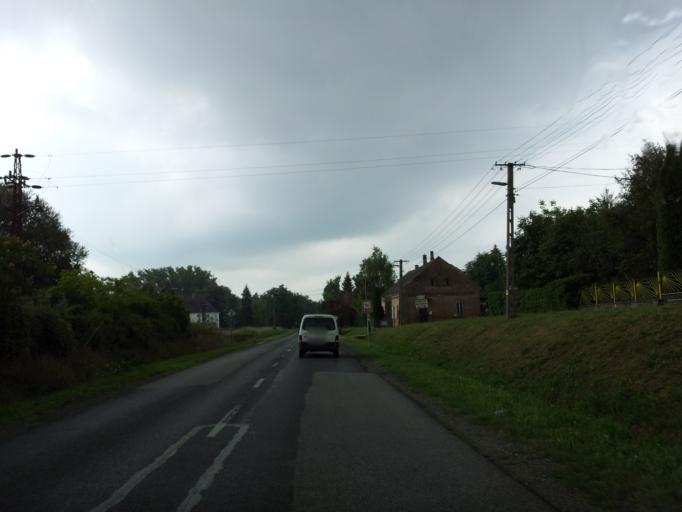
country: HU
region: Tolna
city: Hogyesz
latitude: 46.5034
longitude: 18.4126
